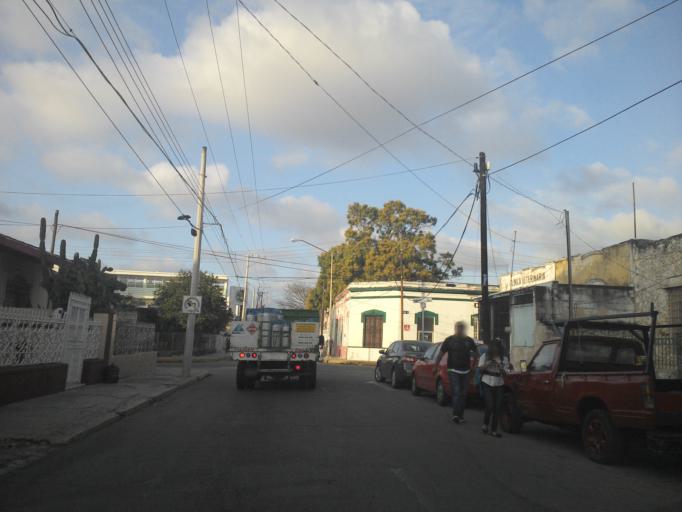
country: MX
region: Yucatan
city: Merida
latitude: 20.9739
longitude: -89.6291
